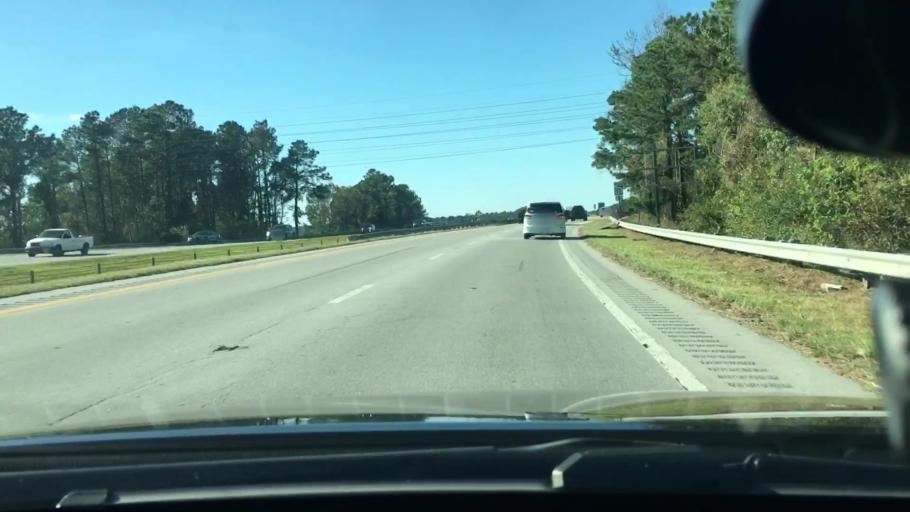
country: US
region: North Carolina
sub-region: Craven County
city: Trent Woods
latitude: 35.1010
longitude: -77.0795
